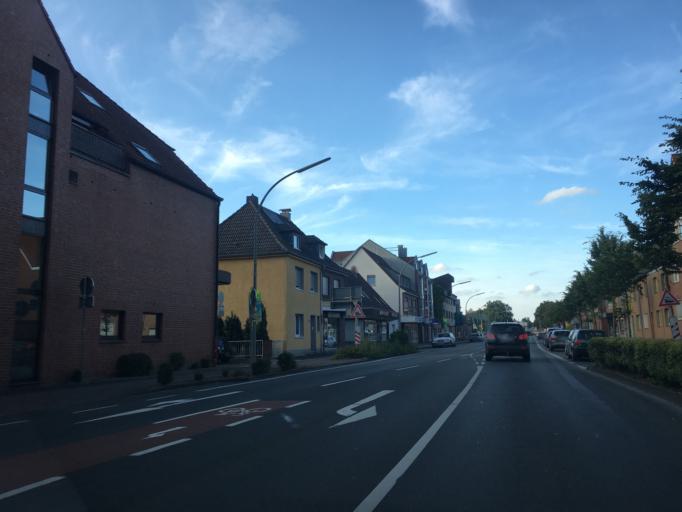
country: DE
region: North Rhine-Westphalia
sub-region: Regierungsbezirk Munster
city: Dulmen
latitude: 51.8330
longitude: 7.2815
